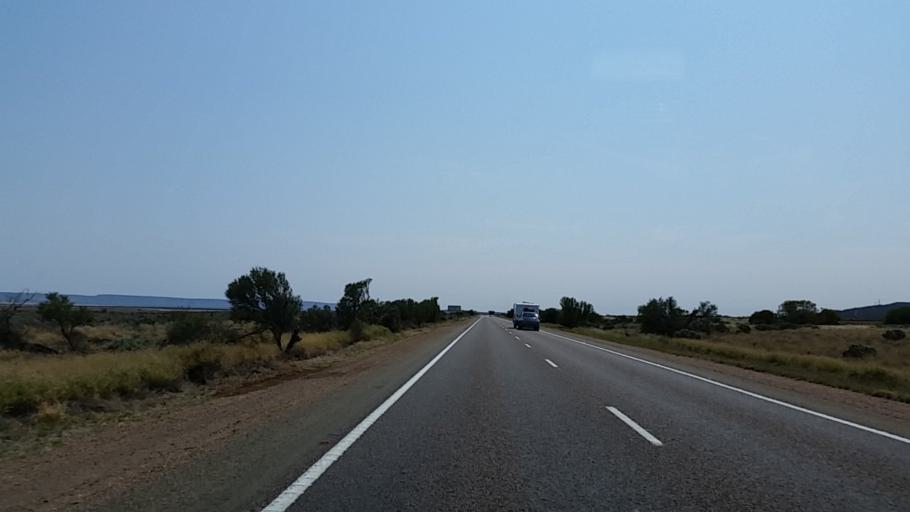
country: AU
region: South Australia
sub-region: Port Augusta
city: Port Augusta
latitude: -32.8127
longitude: 137.9690
